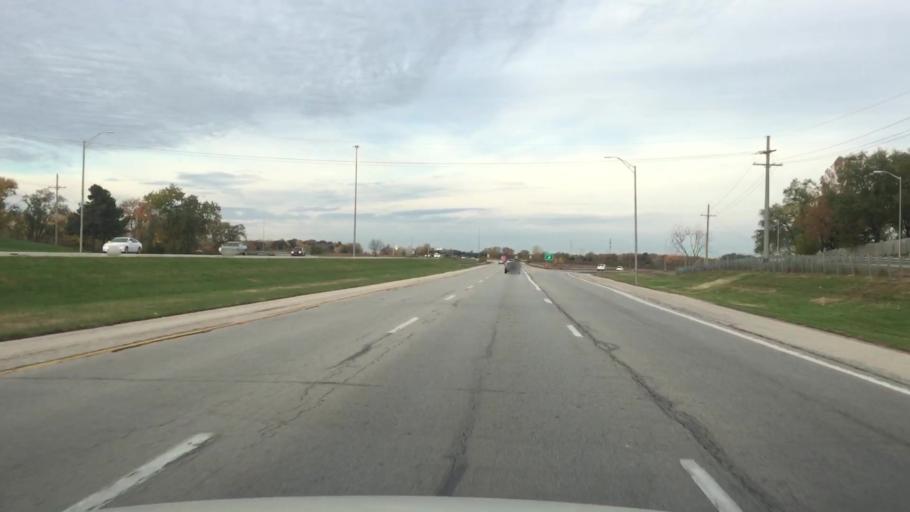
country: US
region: Kansas
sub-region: Johnson County
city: Shawnee
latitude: 39.0097
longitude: -94.7765
